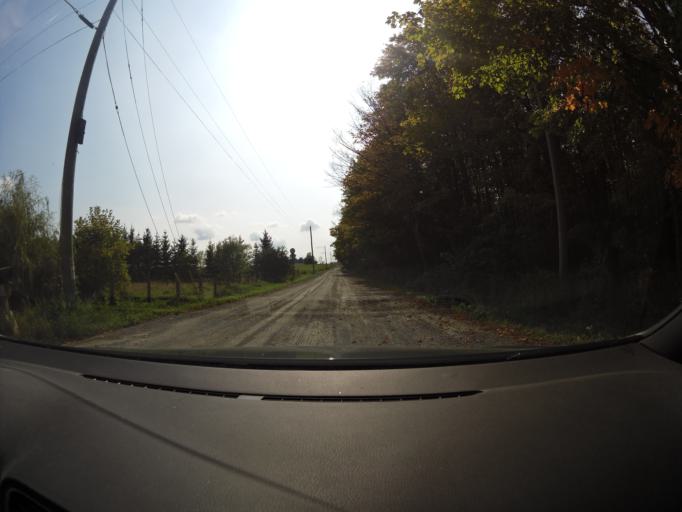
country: CA
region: Ontario
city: Arnprior
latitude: 45.4256
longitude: -76.2392
